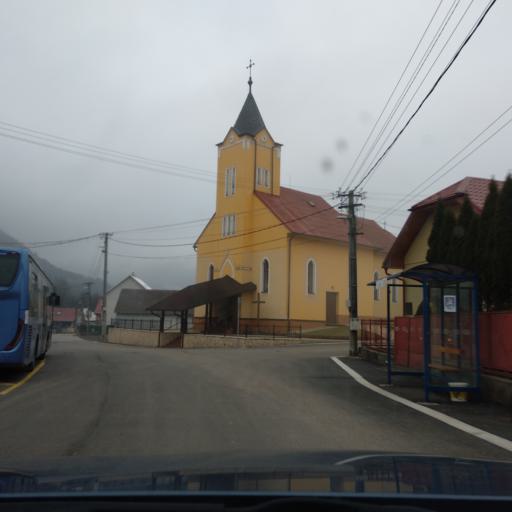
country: SK
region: Nitriansky
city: Ilava
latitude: 48.9111
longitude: 18.2961
